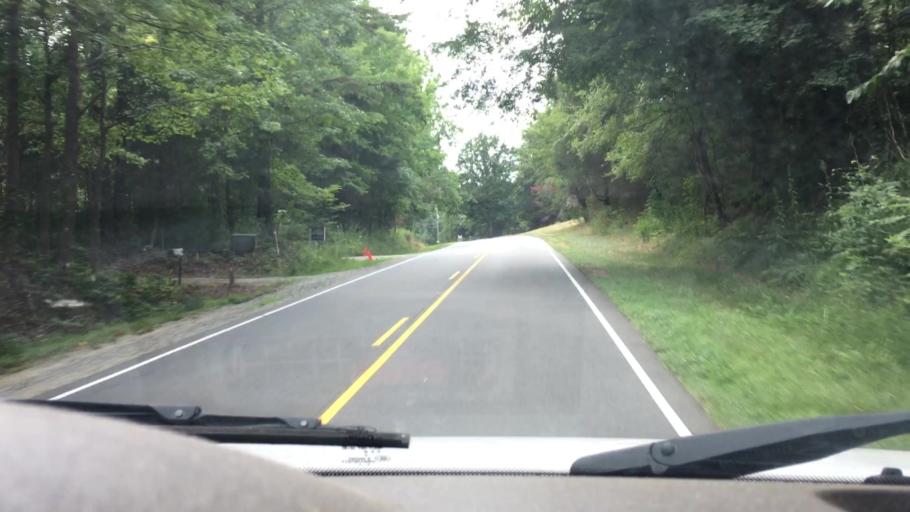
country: US
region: North Carolina
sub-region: Gaston County
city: Davidson
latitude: 35.4738
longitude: -80.7956
